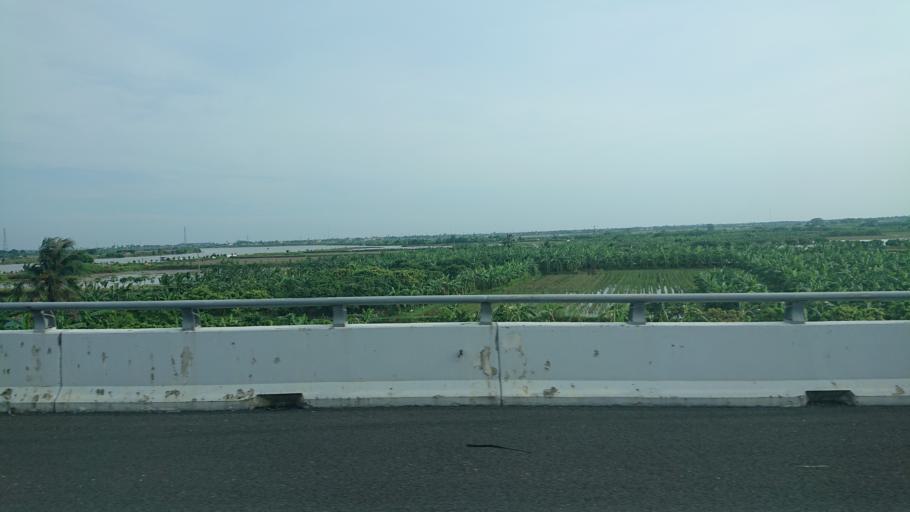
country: VN
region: Hai Phong
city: An Lao
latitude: 20.8091
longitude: 106.5094
